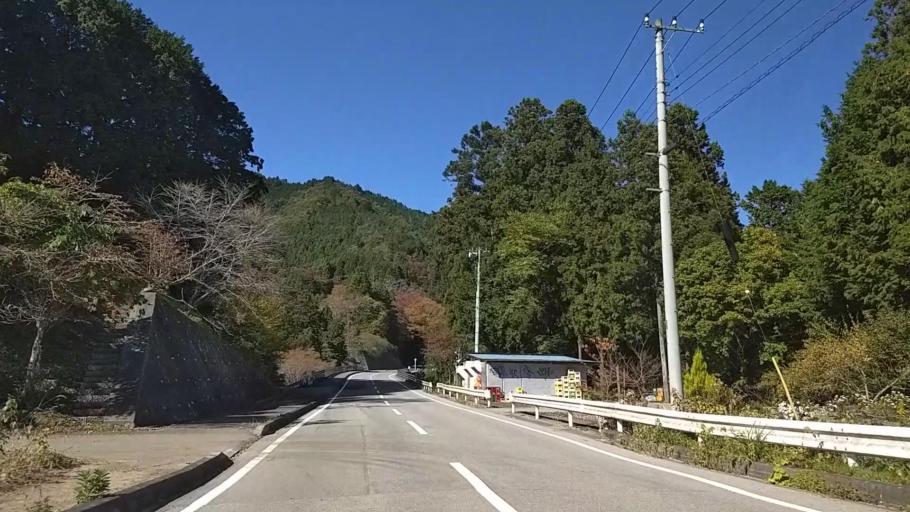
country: JP
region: Yamanashi
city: Uenohara
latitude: 35.6631
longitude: 139.0882
